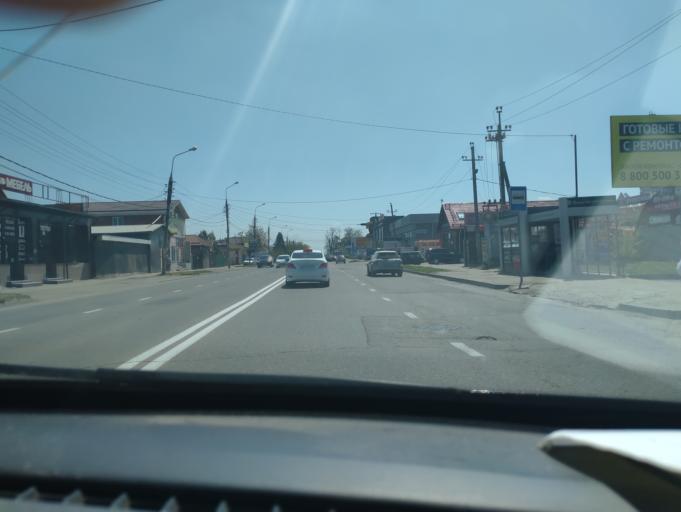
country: RU
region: Krasnodarskiy
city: Krasnodar
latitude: 45.0934
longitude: 39.0138
